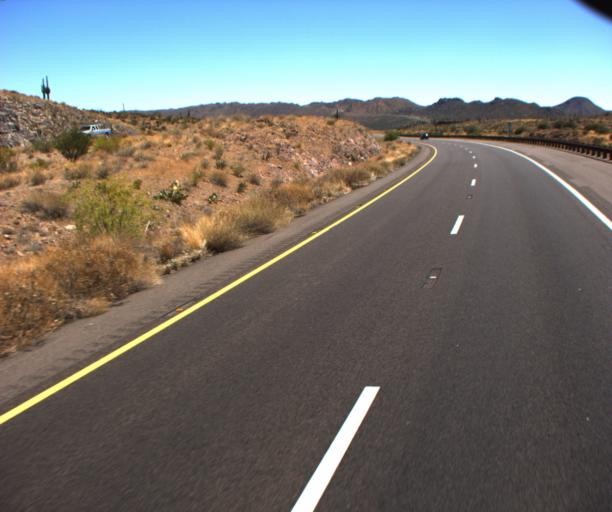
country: US
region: Arizona
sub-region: Maricopa County
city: Rio Verde
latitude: 33.7483
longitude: -111.5036
